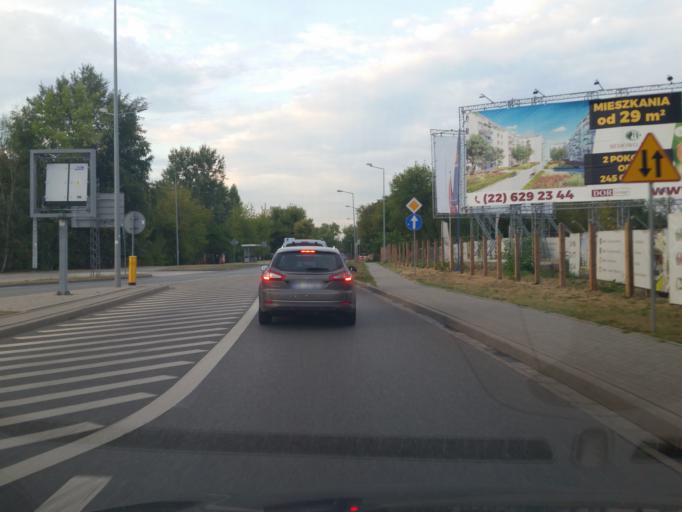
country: PL
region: Masovian Voivodeship
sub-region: Warszawa
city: Bemowo
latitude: 52.2450
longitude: 20.8976
